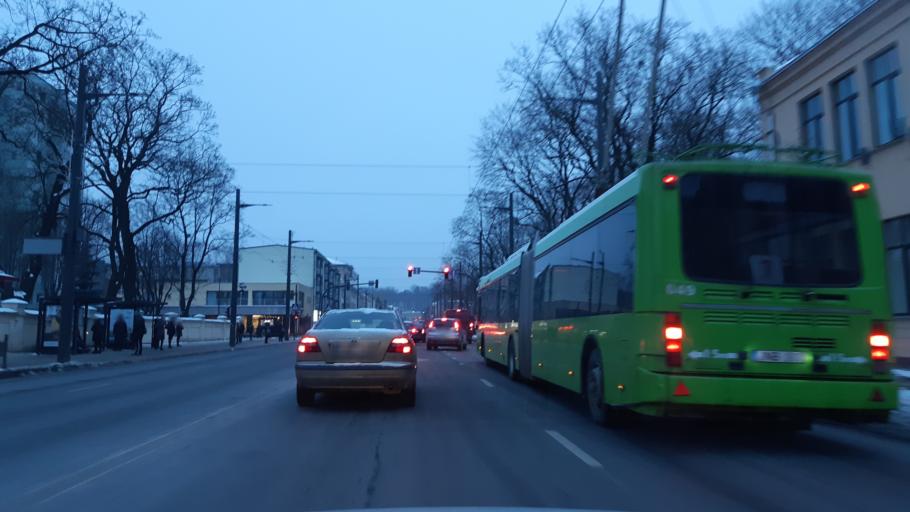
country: LT
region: Kauno apskritis
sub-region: Kaunas
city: Aleksotas
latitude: 54.8912
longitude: 23.9248
